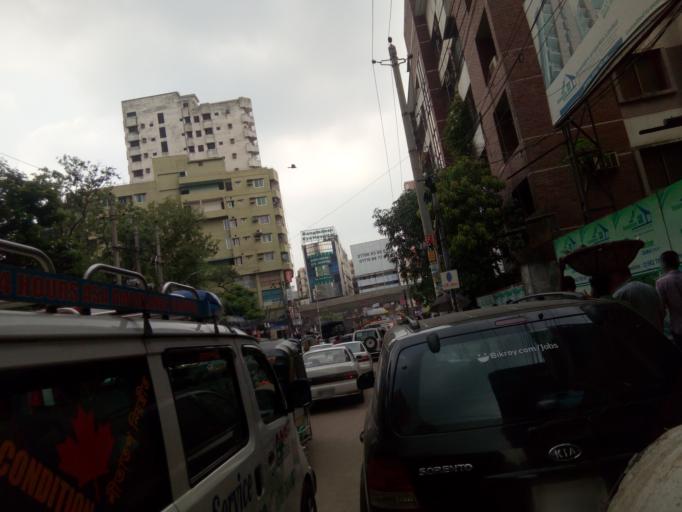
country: BD
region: Dhaka
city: Paltan
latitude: 23.7420
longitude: 90.4106
